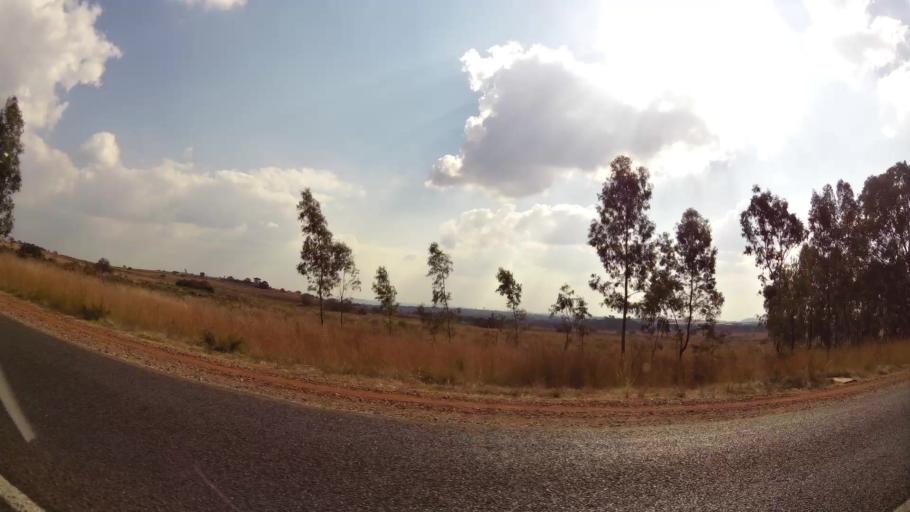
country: ZA
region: Gauteng
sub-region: City of Tshwane Metropolitan Municipality
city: Centurion
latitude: -25.8653
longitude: 28.2378
